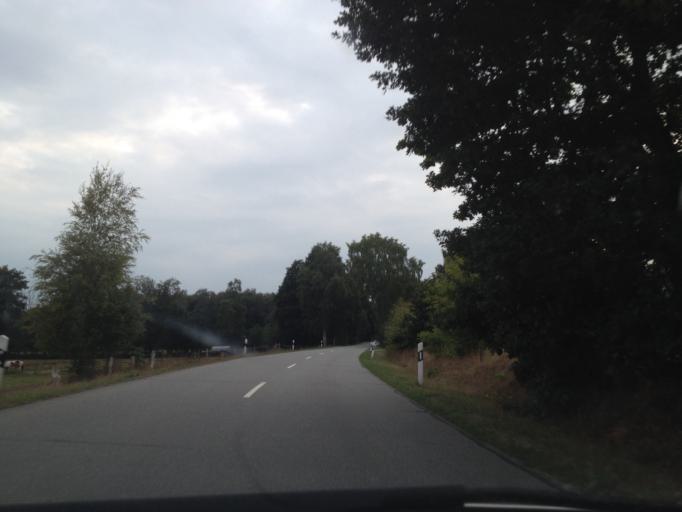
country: DE
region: Schleswig-Holstein
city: Daldorf
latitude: 54.0117
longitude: 10.2297
